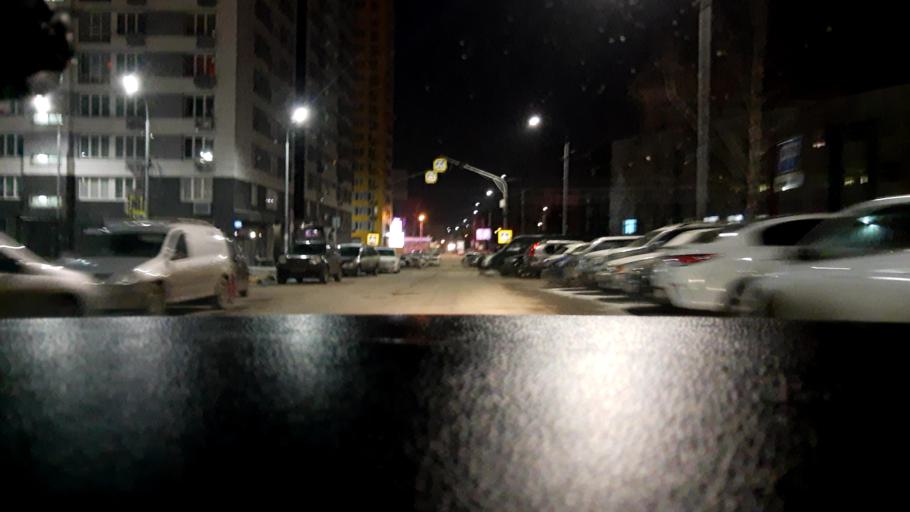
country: RU
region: Moskovskaya
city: Vidnoye
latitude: 55.5426
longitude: 37.7129
